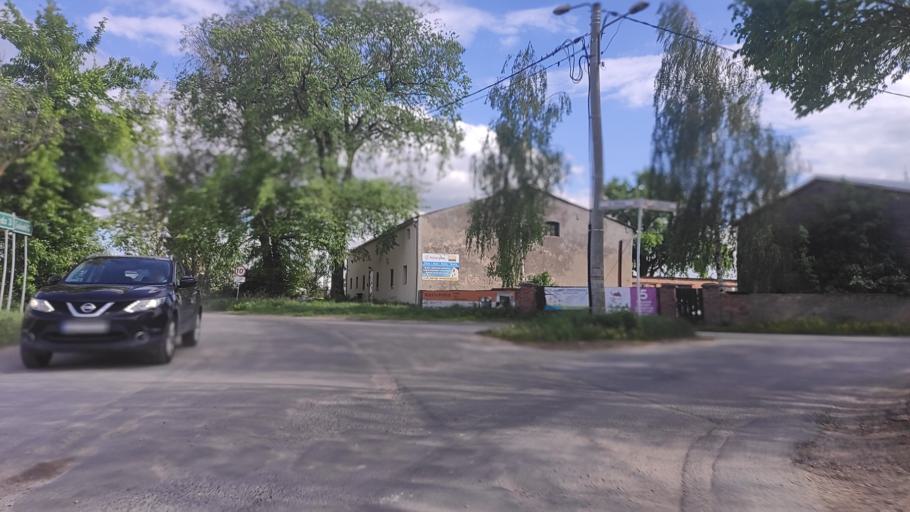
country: PL
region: Greater Poland Voivodeship
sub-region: Powiat poznanski
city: Swarzedz
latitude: 52.3906
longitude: 17.1192
